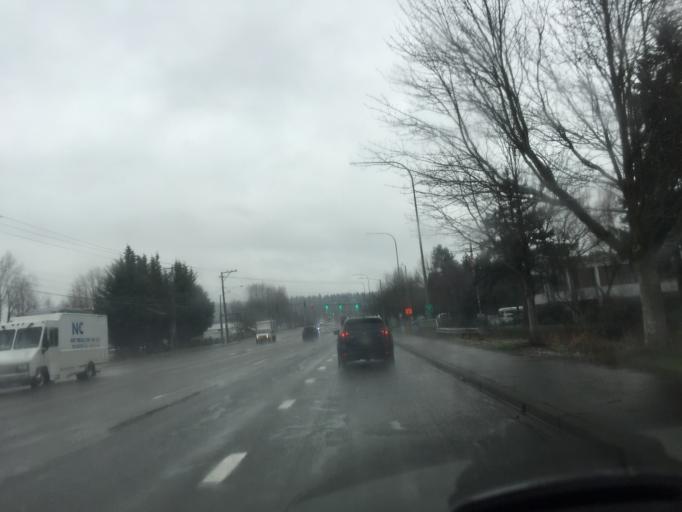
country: US
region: Washington
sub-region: King County
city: Kent
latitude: 47.4117
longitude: -122.2400
